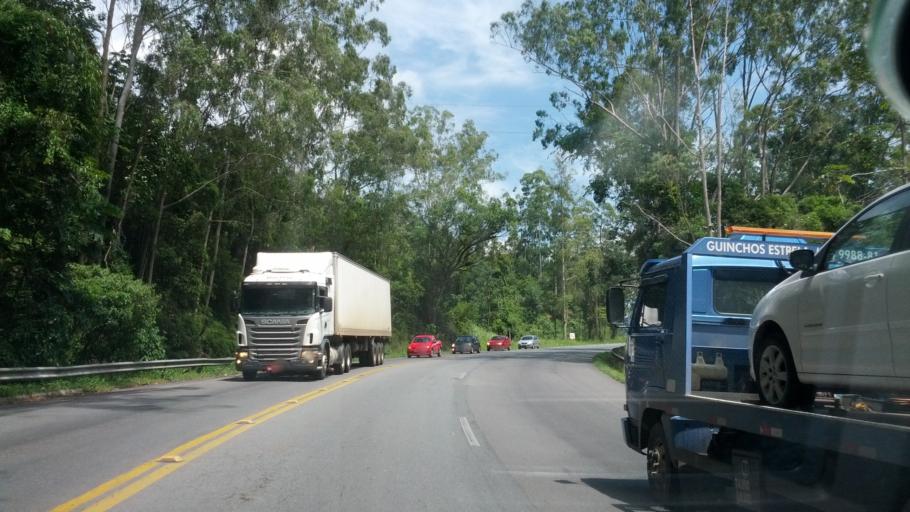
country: BR
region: Santa Catarina
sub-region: Ibirama
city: Ibirama
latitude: -27.0960
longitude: -49.5271
